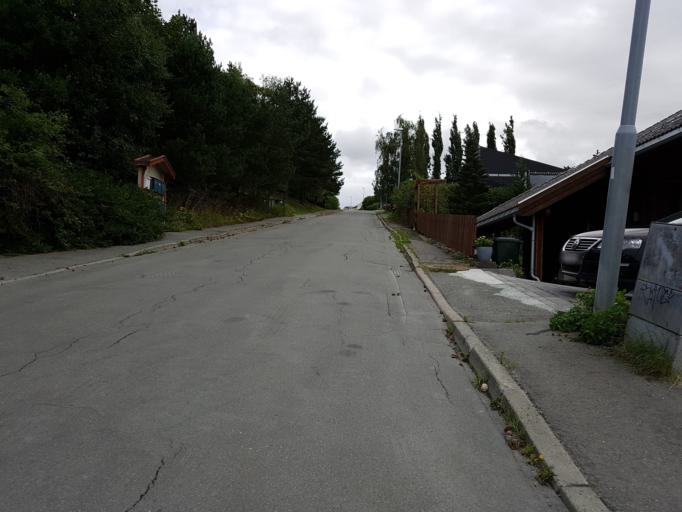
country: NO
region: Sor-Trondelag
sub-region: Trondheim
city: Trondheim
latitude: 63.3960
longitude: 10.4159
